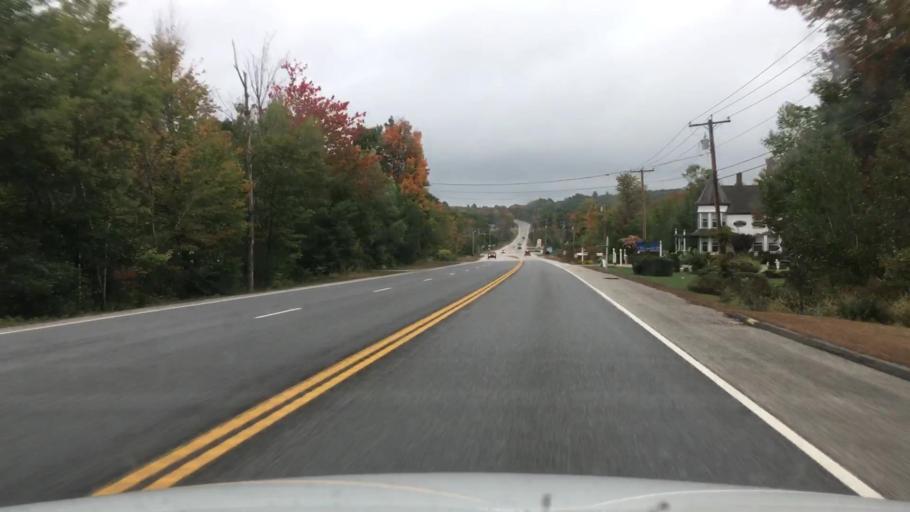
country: US
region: Maine
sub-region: Androscoggin County
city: Poland
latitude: 44.0100
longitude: -70.3622
